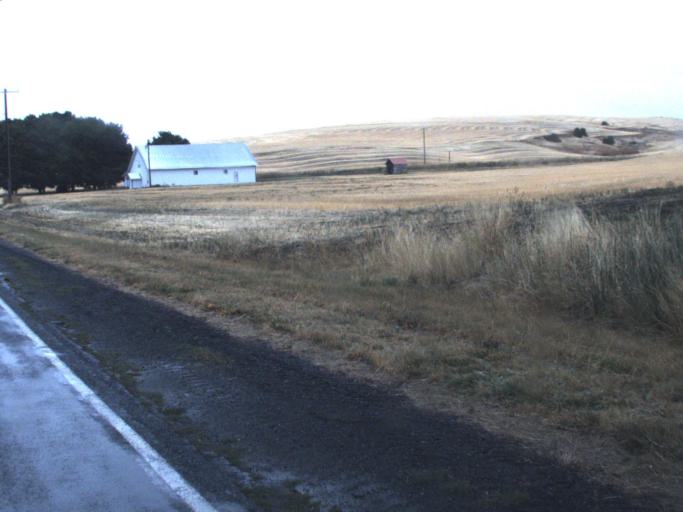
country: US
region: Washington
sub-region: Whitman County
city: Colfax
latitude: 47.0504
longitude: -117.5176
